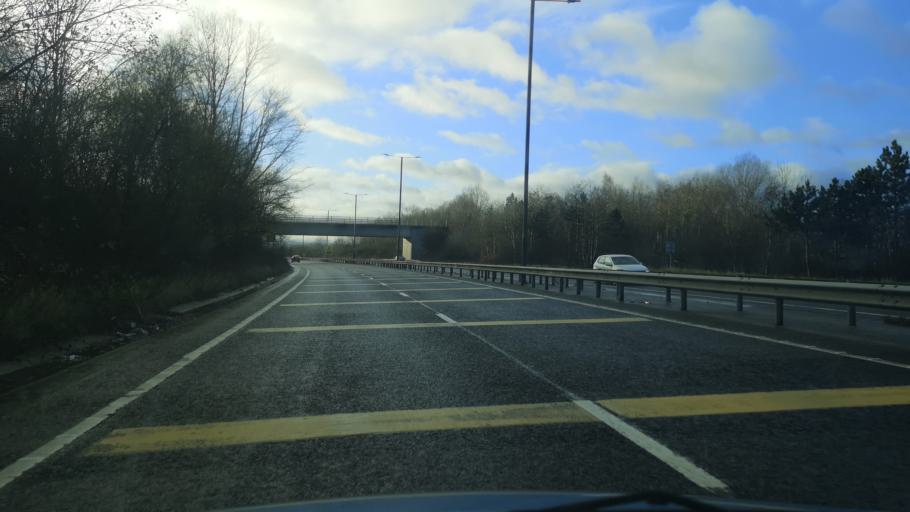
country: GB
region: England
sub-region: Barnsley
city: Hoyland Nether
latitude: 53.5092
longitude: -1.4553
